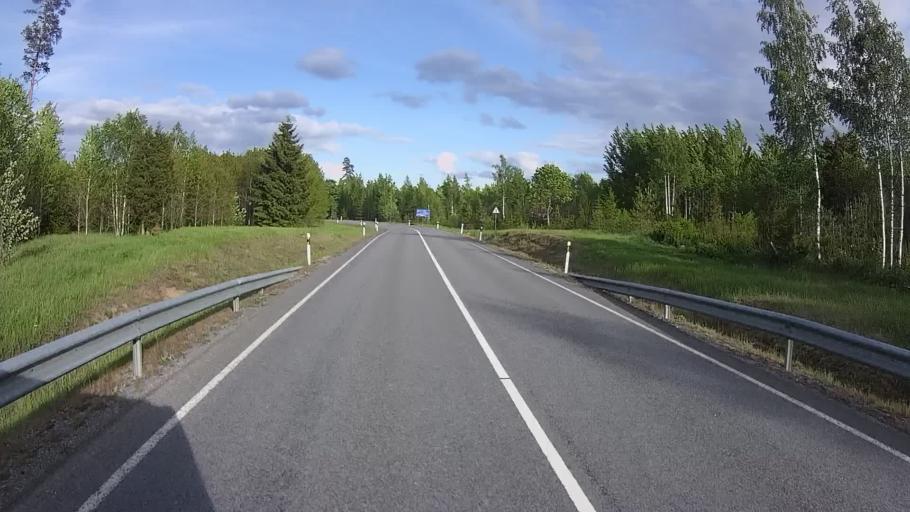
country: EE
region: Jogevamaa
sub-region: Mustvee linn
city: Mustvee
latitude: 59.0489
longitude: 27.0291
